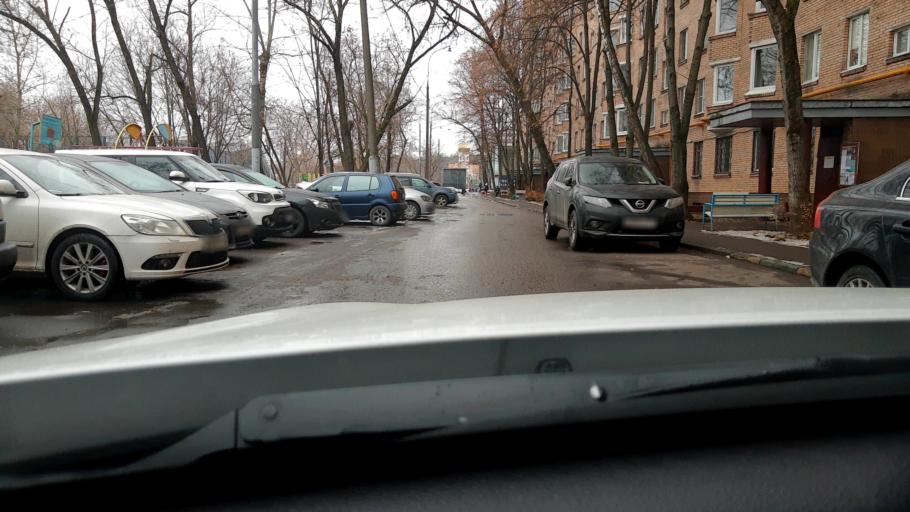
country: RU
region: Moscow
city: Pokrovskoye-Streshnevo
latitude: 55.8101
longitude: 37.4571
